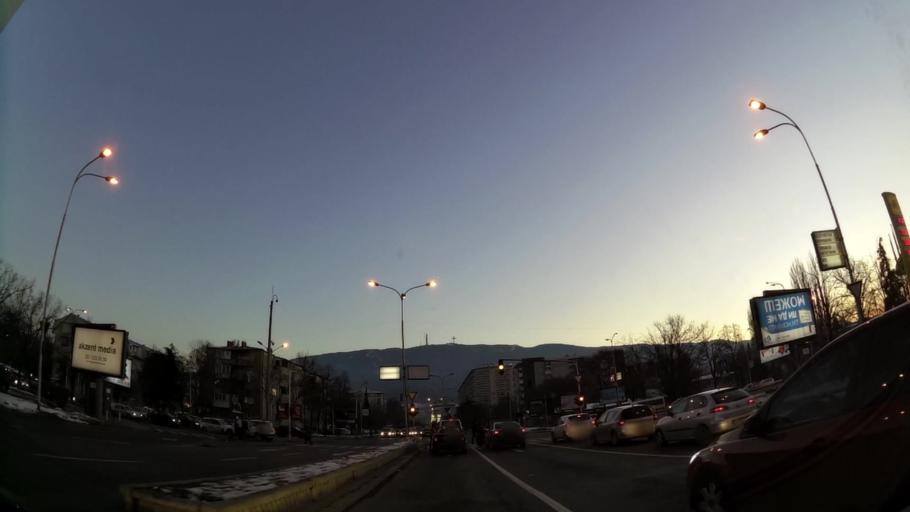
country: MK
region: Karpos
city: Skopje
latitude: 42.0022
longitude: 21.4048
